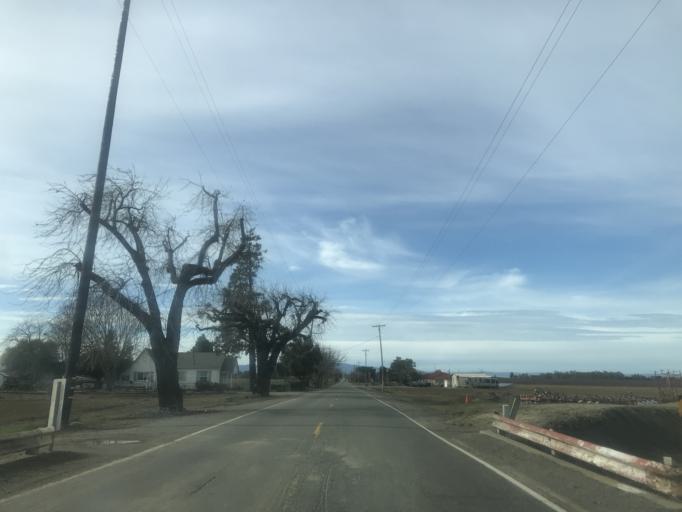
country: US
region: California
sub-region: Yolo County
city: Woodland
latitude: 38.6634
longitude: -121.8435
